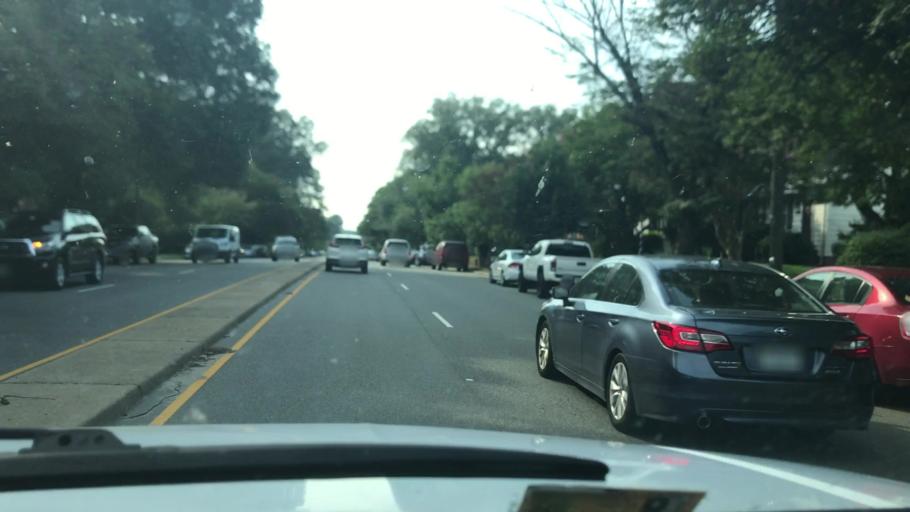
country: US
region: Virginia
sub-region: Henrico County
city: Dumbarton
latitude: 37.5707
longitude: -77.4983
